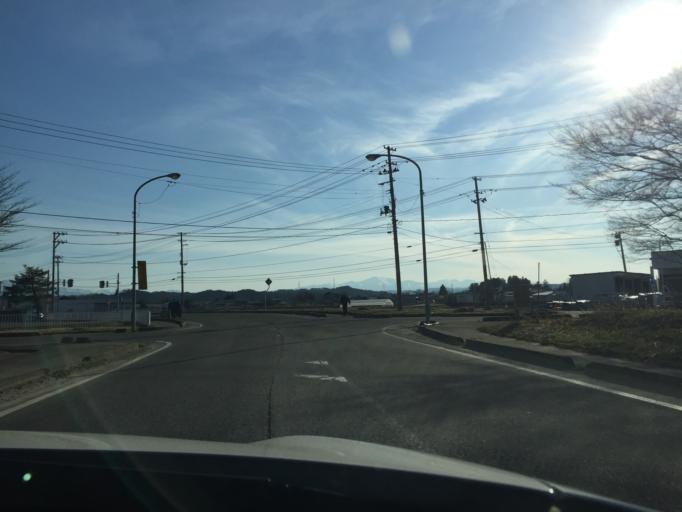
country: JP
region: Yamagata
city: Nagai
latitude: 38.0125
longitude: 140.0545
